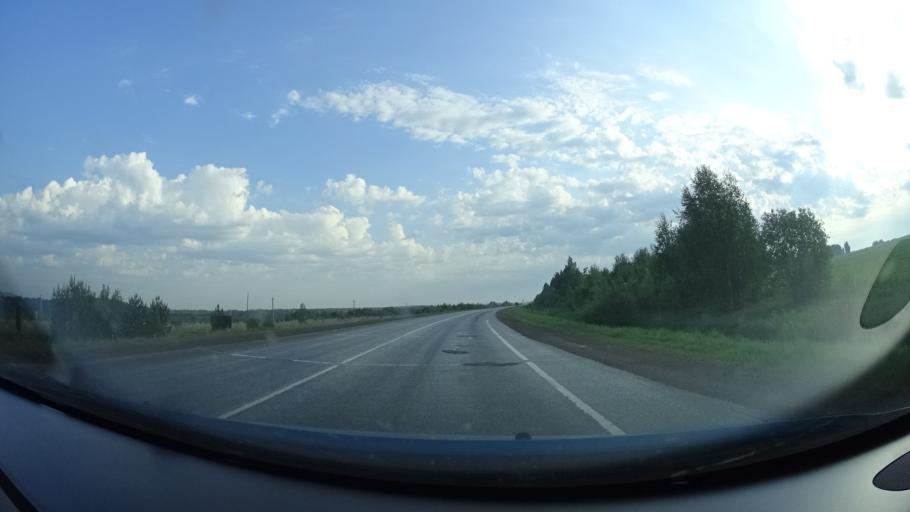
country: RU
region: Perm
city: Osa
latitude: 57.3347
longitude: 55.5841
